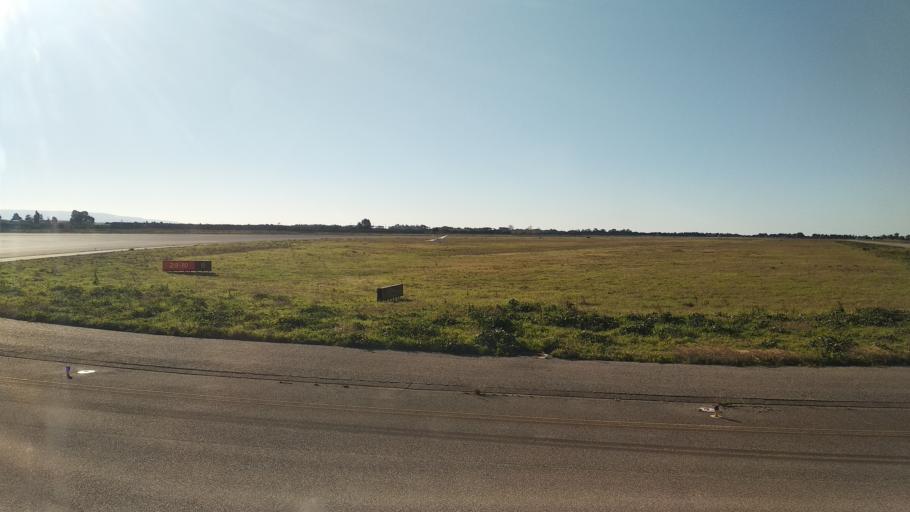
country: IT
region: Calabria
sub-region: Provincia di Catanzaro
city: Santa Eufemia Lamezia
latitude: 38.9063
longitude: 16.2503
